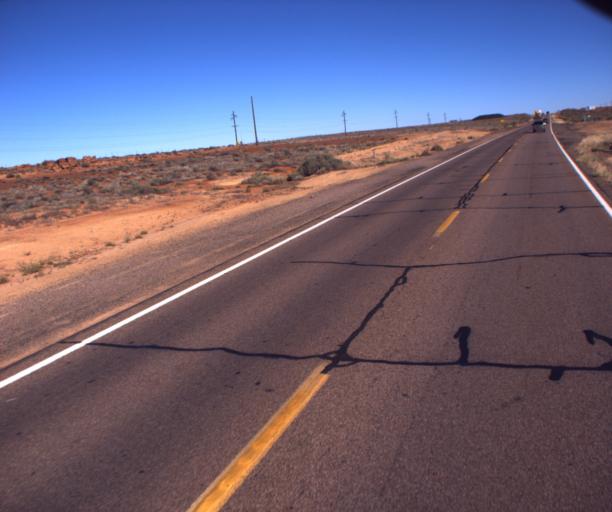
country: US
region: Arizona
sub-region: Navajo County
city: Holbrook
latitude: 34.8787
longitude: -110.1626
